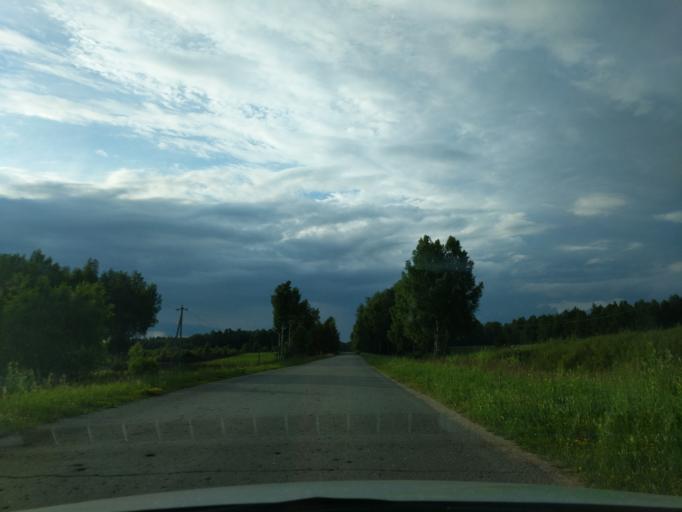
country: RU
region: Kaluga
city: Myatlevo
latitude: 54.8170
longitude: 35.6755
